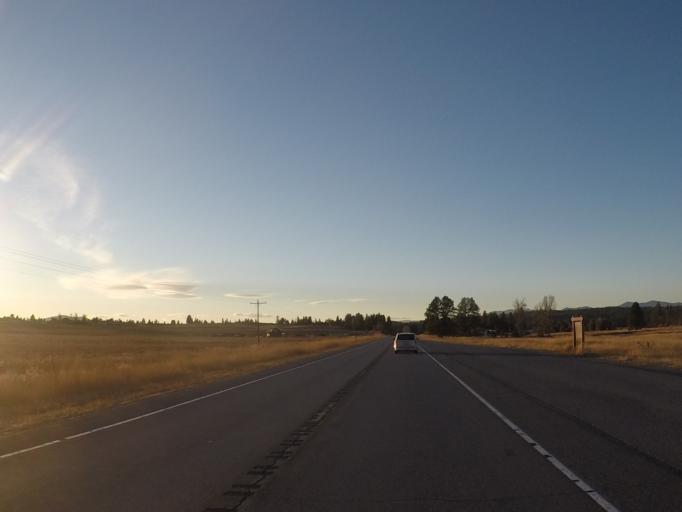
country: US
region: Montana
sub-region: Lewis and Clark County
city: Lincoln
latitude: 46.9946
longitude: -113.0235
